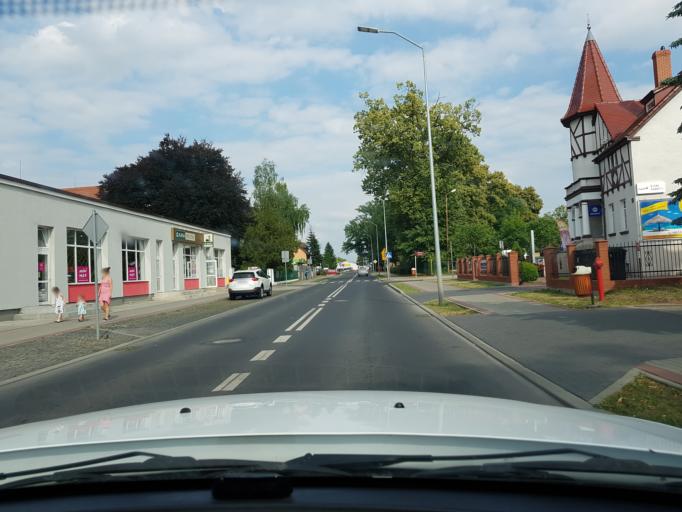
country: PL
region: West Pomeranian Voivodeship
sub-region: Powiat gryfinski
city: Chojna
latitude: 52.9605
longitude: 14.4378
